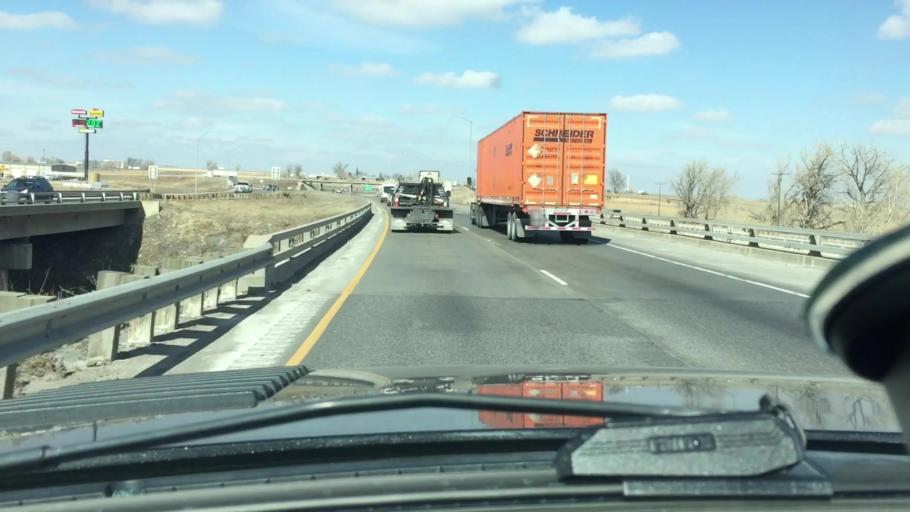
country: US
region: Colorado
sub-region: Weld County
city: Mead
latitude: 40.3008
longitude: -104.9815
